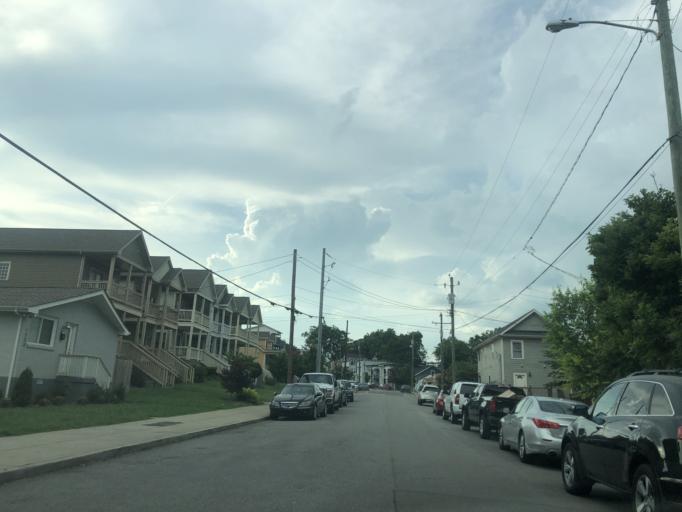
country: US
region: Tennessee
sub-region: Davidson County
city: Nashville
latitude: 36.1828
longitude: -86.7946
